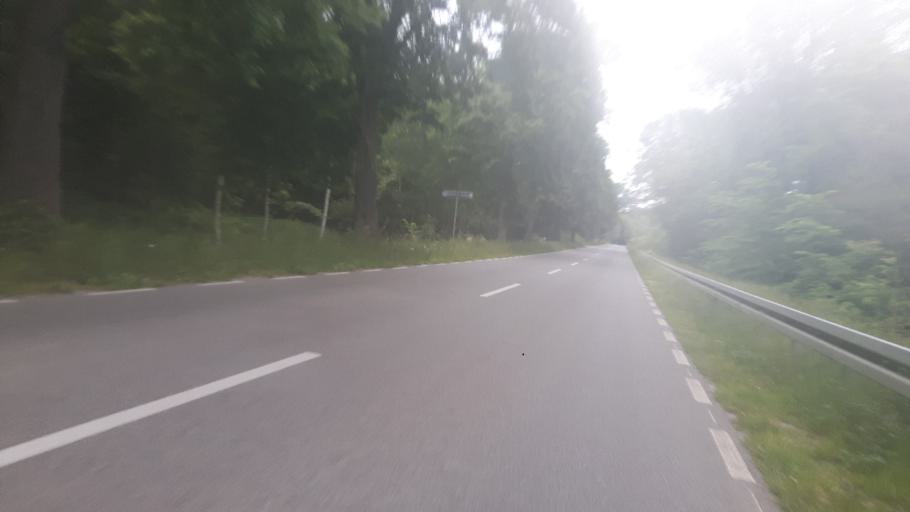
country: PL
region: Warmian-Masurian Voivodeship
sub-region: Powiat elblaski
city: Elblag
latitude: 54.2665
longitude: 19.4152
